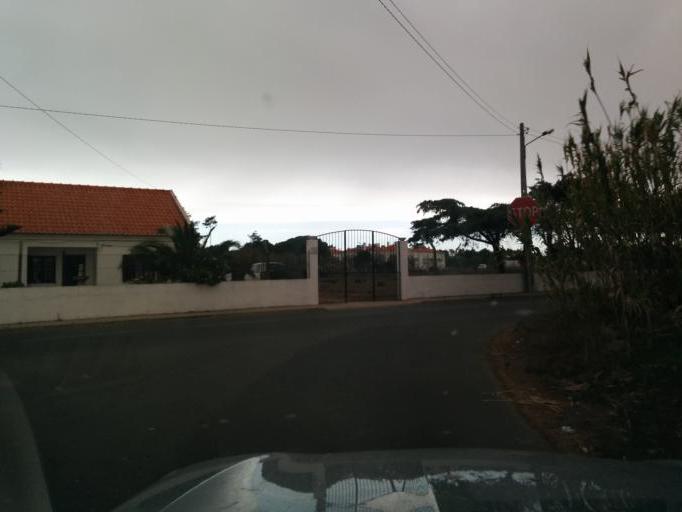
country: PT
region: Beja
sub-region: Odemira
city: Vila Nova de Milfontes
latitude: 37.7319
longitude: -8.7792
